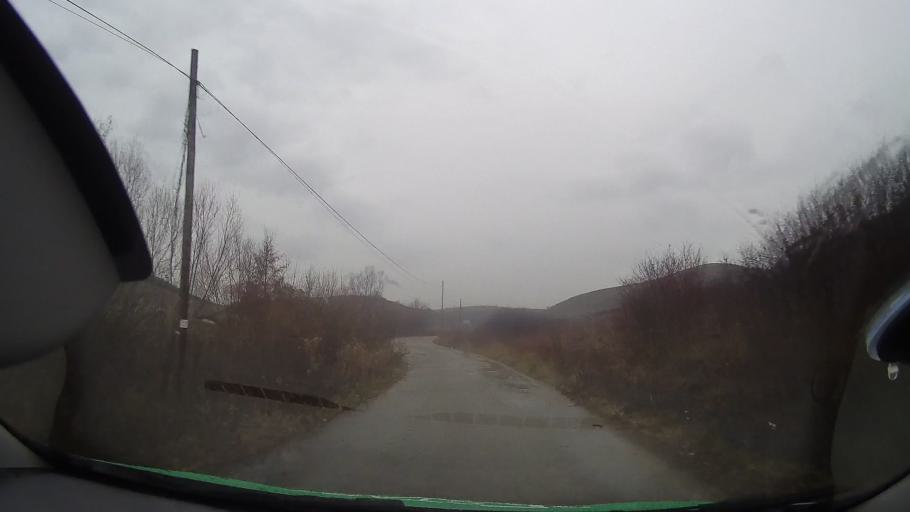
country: RO
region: Bihor
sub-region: Comuna Uileacu de Beius
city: Uileacu de Beius
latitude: 46.6911
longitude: 22.2174
